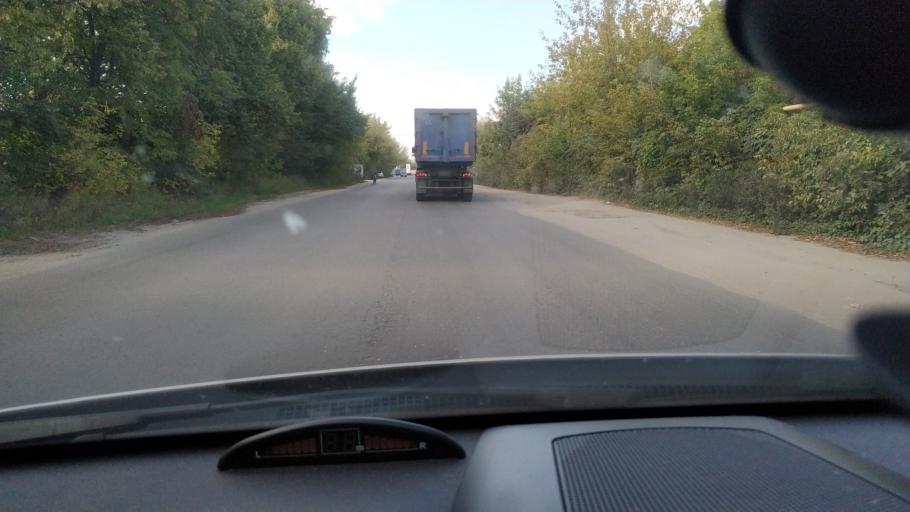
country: RU
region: Rjazan
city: Ryazan'
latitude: 54.6623
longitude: 39.6296
